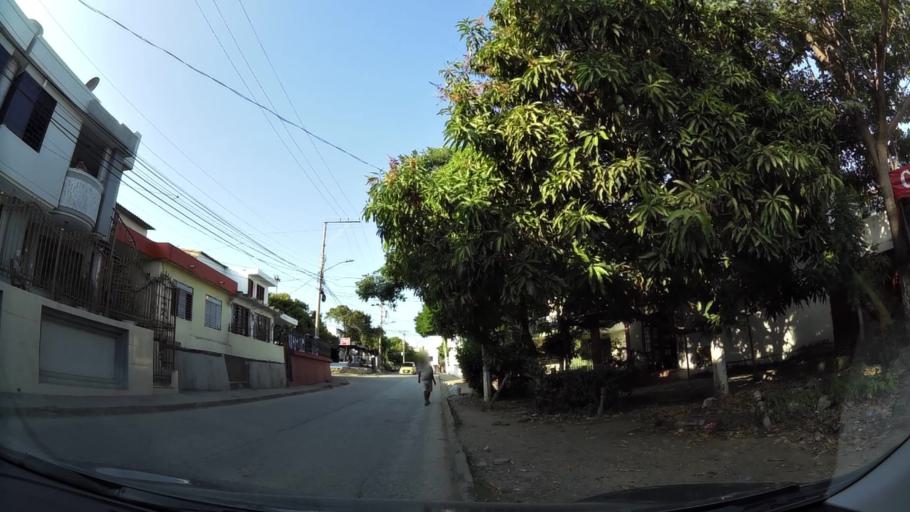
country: CO
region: Bolivar
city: Cartagena
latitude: 10.3840
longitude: -75.4793
